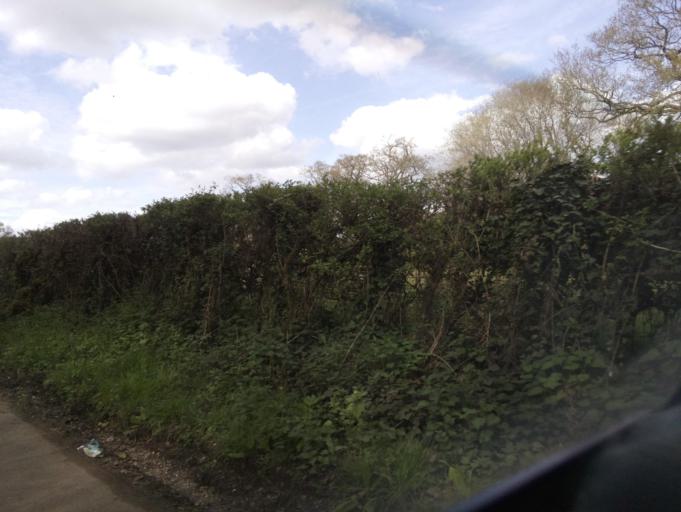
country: GB
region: England
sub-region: Hampshire
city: Romsey
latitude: 51.0262
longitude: -1.4934
